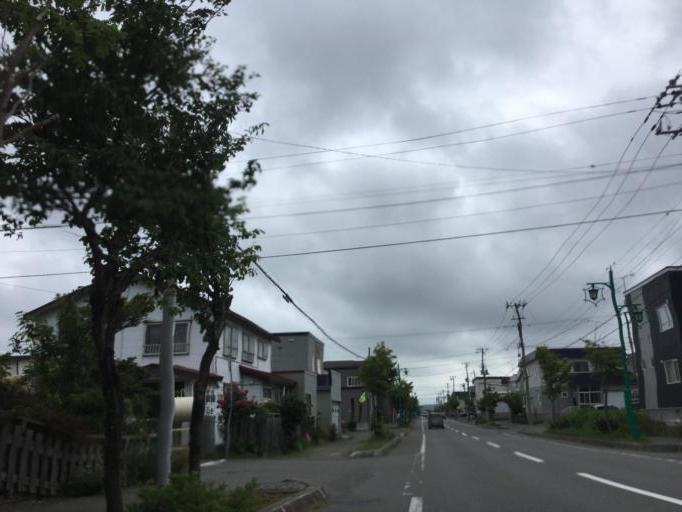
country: JP
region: Hokkaido
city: Wakkanai
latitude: 45.3905
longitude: 141.6997
